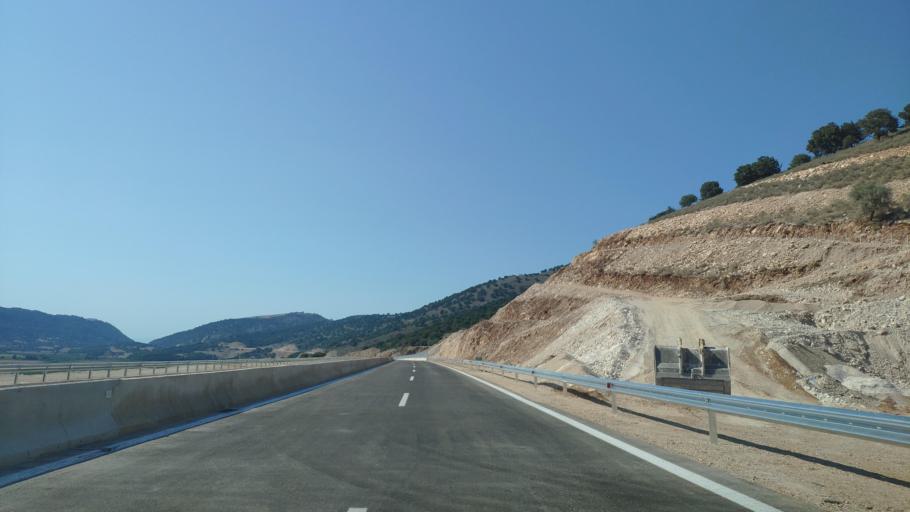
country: GR
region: West Greece
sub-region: Nomos Aitolias kai Akarnanias
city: Katouna
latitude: 38.8199
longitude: 21.1261
